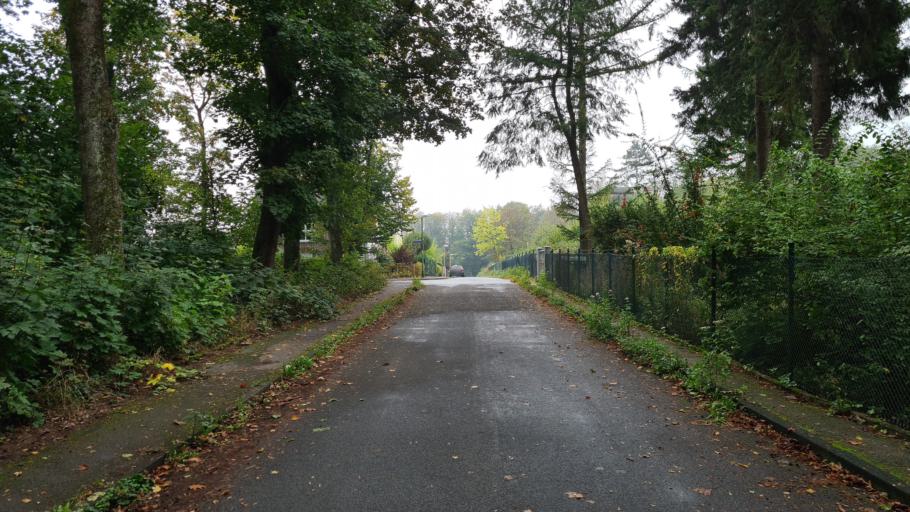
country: DE
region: North Rhine-Westphalia
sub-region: Regierungsbezirk Dusseldorf
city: Essen
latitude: 51.4142
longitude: 7.0006
